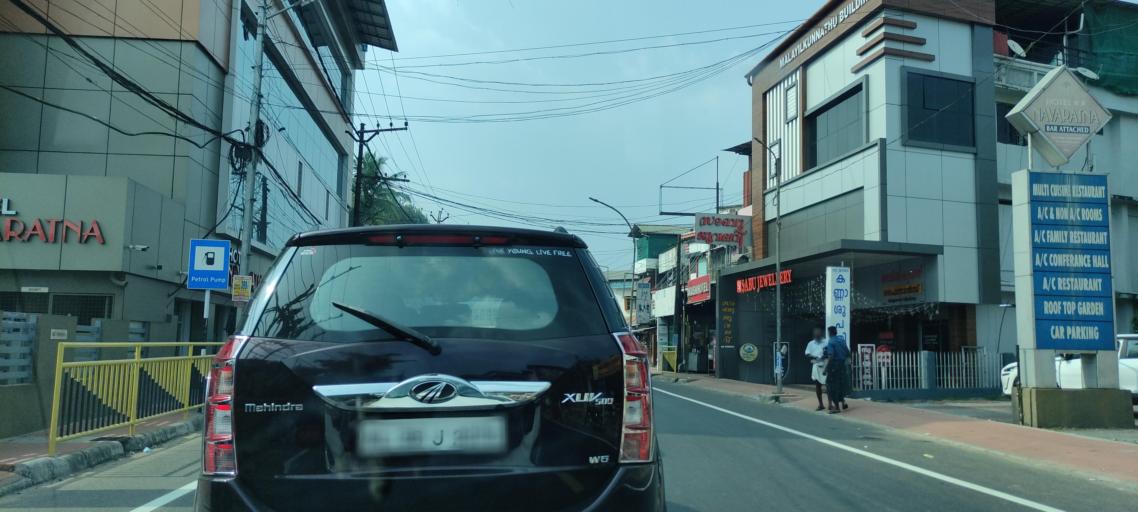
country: IN
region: Kerala
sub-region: Alappuzha
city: Chengannur
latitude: 9.3200
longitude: 76.6110
